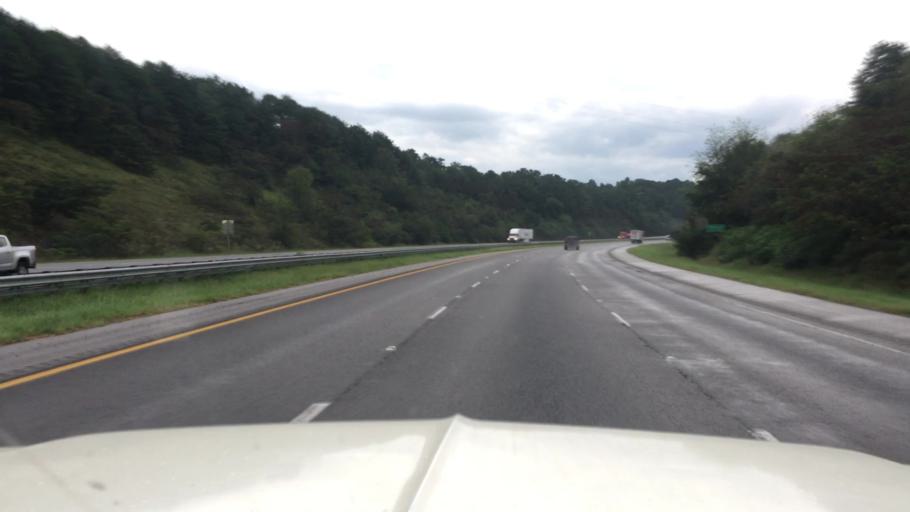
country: US
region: Alabama
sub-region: Jefferson County
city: Gardendale
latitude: 33.6842
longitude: -86.8287
